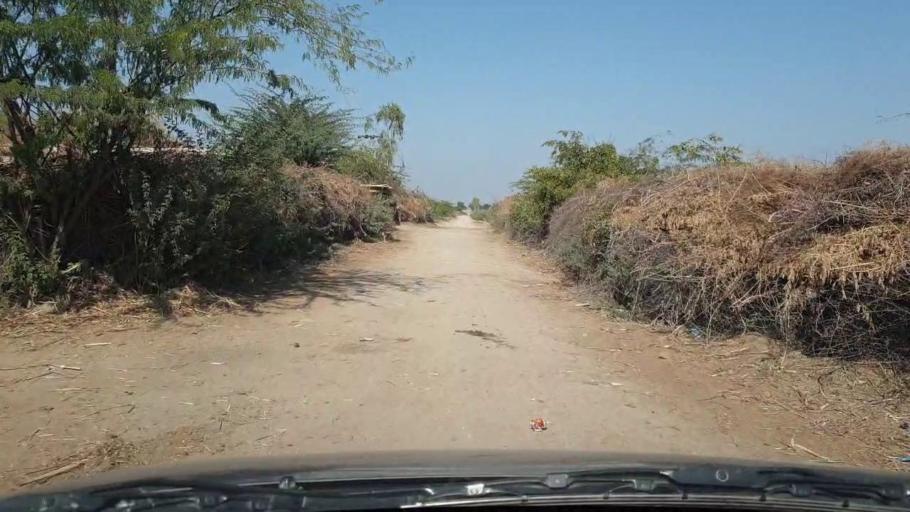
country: PK
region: Sindh
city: Samaro
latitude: 25.2034
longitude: 69.2858
